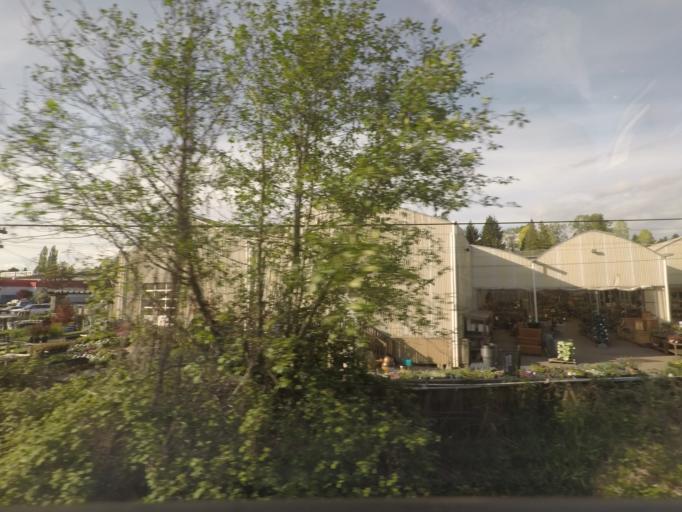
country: CA
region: British Columbia
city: Burnaby
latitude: 49.2617
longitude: -122.9740
